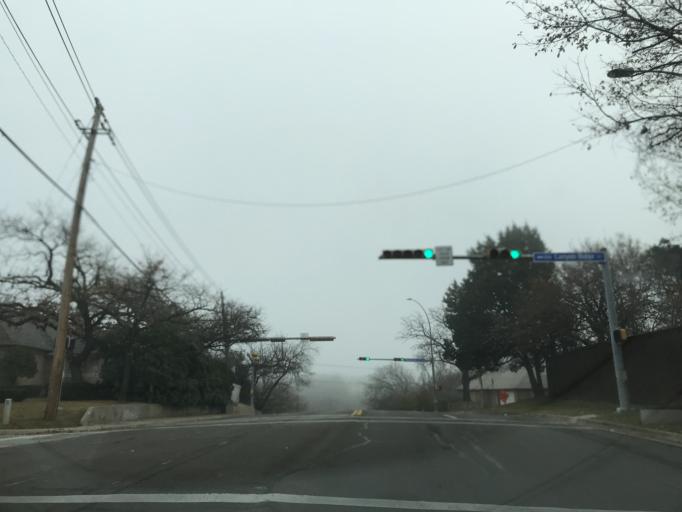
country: US
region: Texas
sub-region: Tarrant County
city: Arlington
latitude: 32.7745
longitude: -97.0894
